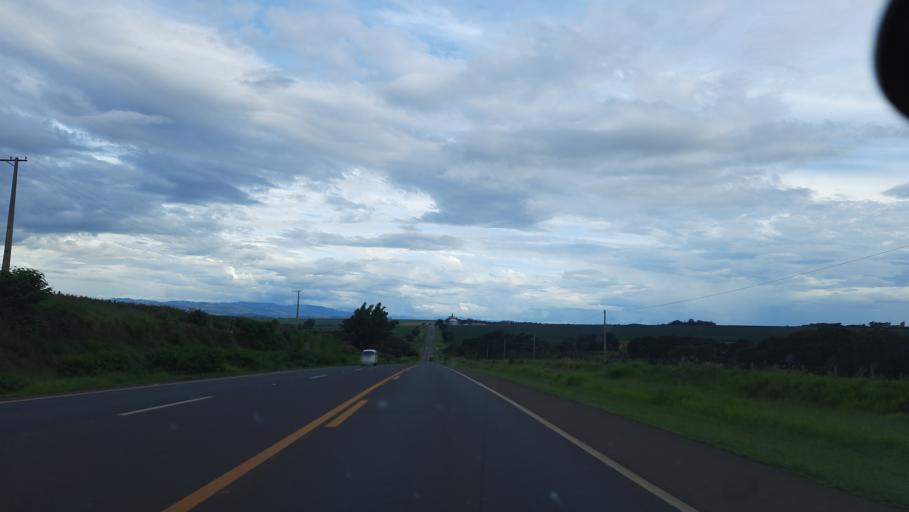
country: BR
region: Sao Paulo
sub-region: Casa Branca
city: Casa Branca
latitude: -21.7908
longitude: -47.0371
